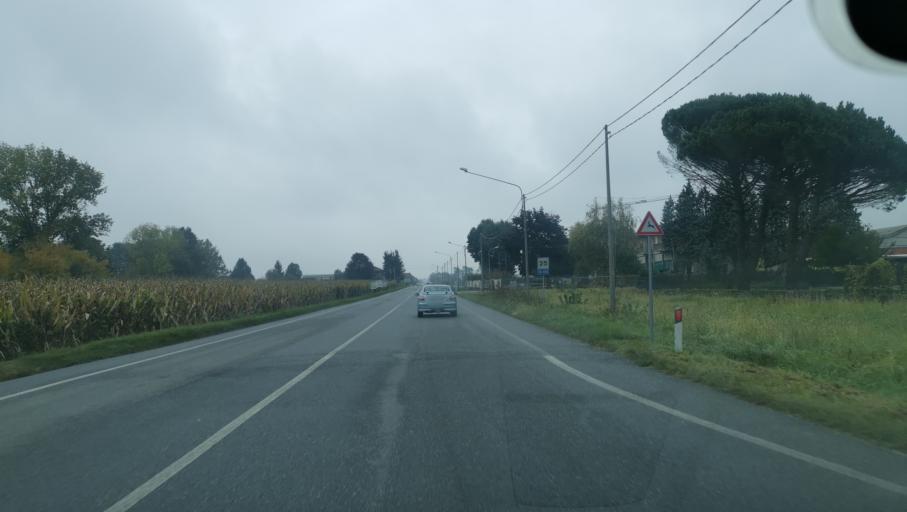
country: IT
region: Piedmont
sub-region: Provincia di Biella
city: Vergnasco
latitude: 45.5022
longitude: 8.0838
